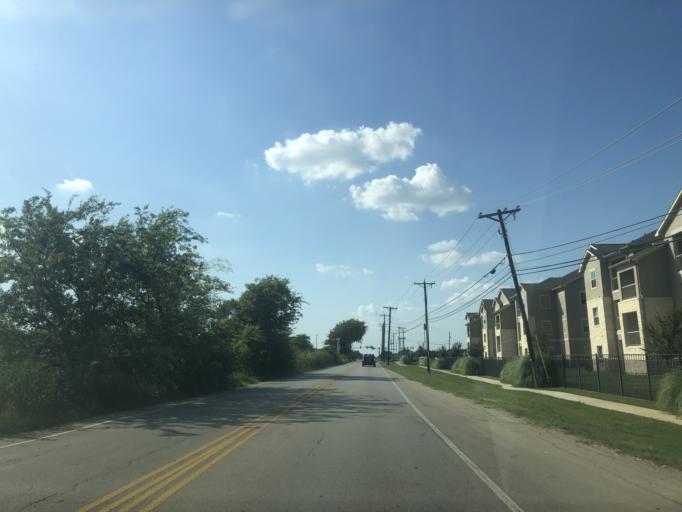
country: US
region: Texas
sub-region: Tarrant County
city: Saginaw
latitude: 32.8455
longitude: -97.3848
